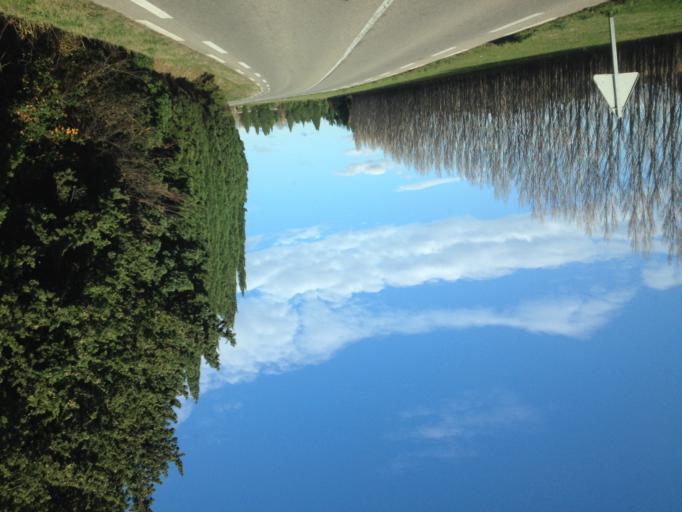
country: FR
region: Provence-Alpes-Cote d'Azur
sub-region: Departement du Vaucluse
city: Orange
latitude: 44.1294
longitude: 4.7829
